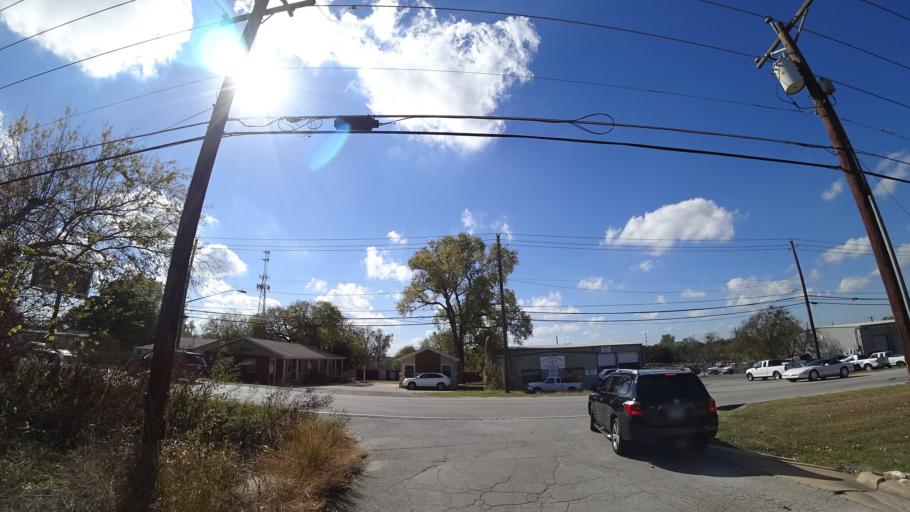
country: US
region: Texas
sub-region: Travis County
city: Wells Branch
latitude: 30.4372
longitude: -97.6912
